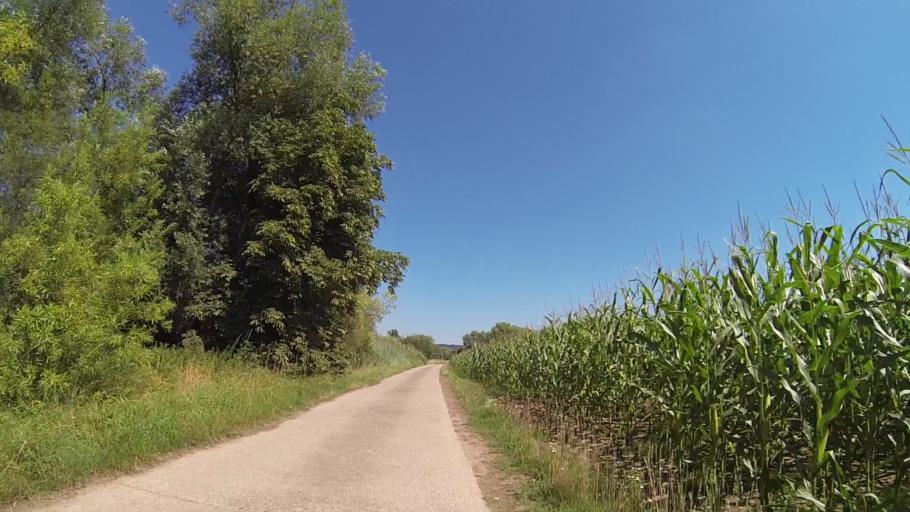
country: LU
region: Grevenmacher
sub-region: Canton de Remich
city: Remich
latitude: 49.5302
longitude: 6.3599
